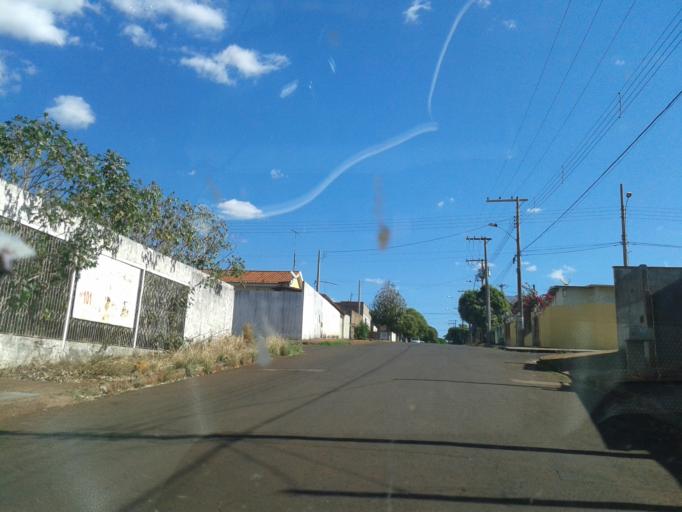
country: BR
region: Minas Gerais
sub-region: Ituiutaba
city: Ituiutaba
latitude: -18.9503
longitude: -49.4591
